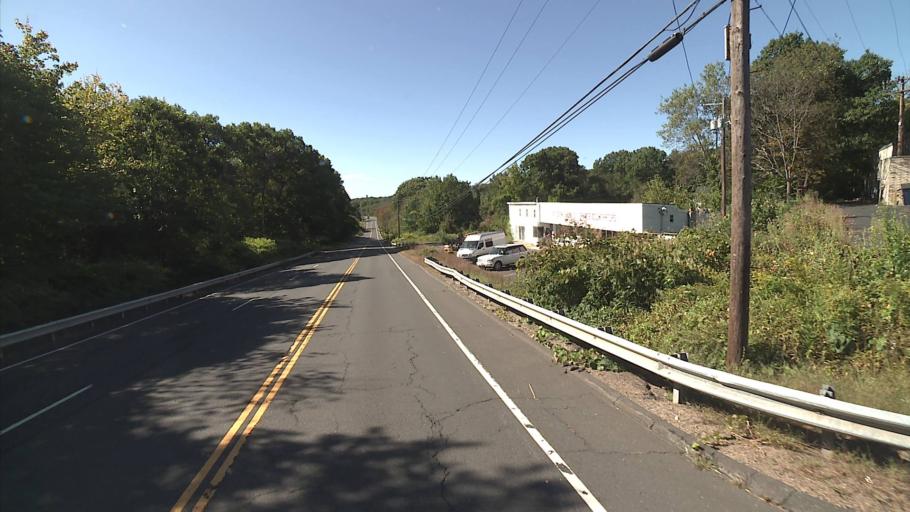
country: US
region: Connecticut
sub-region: New Haven County
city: Wolcott
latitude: 41.6113
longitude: -72.9820
